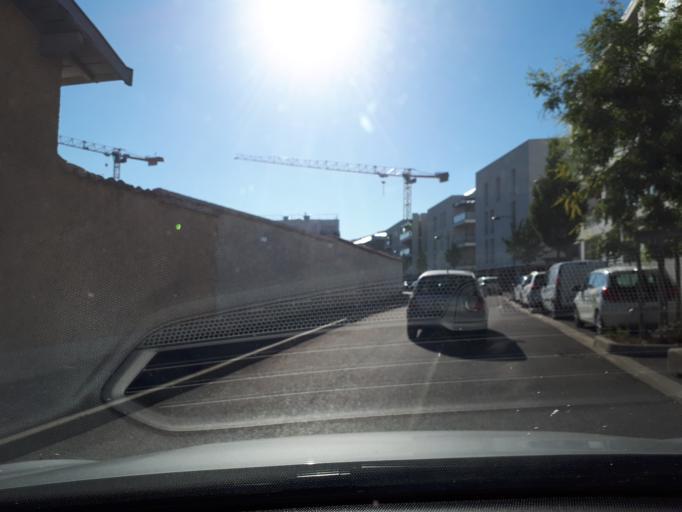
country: FR
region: Rhone-Alpes
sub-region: Departement du Rhone
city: Meyzieu
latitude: 45.7704
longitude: 5.0033
